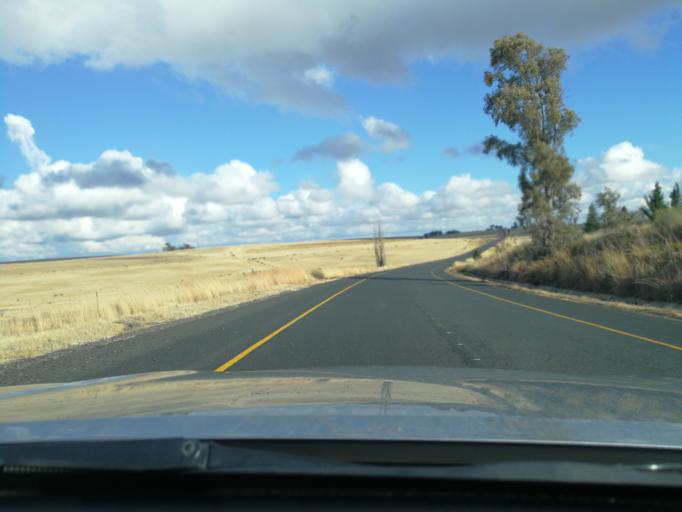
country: ZA
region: Orange Free State
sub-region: Thabo Mofutsanyana District Municipality
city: Reitz
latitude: -27.9041
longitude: 28.3962
